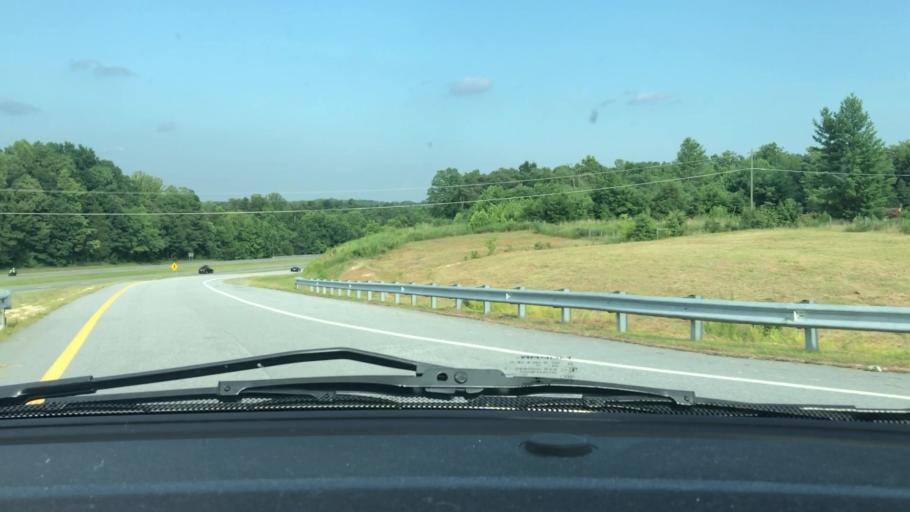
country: US
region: North Carolina
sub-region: Guilford County
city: Forest Oaks
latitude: 35.9619
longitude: -79.7036
